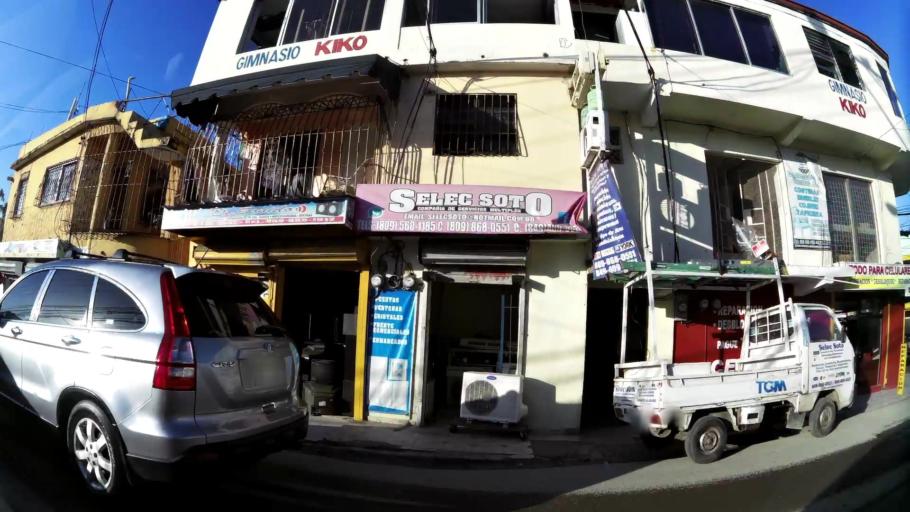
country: DO
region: Nacional
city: Santo Domingo
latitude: 18.4888
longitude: -69.9696
